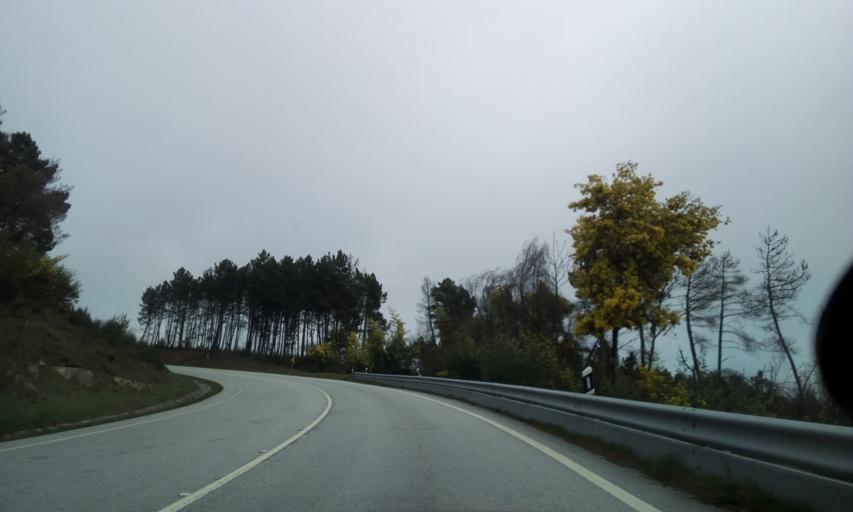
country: PT
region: Guarda
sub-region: Celorico da Beira
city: Celorico da Beira
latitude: 40.6903
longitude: -7.4683
